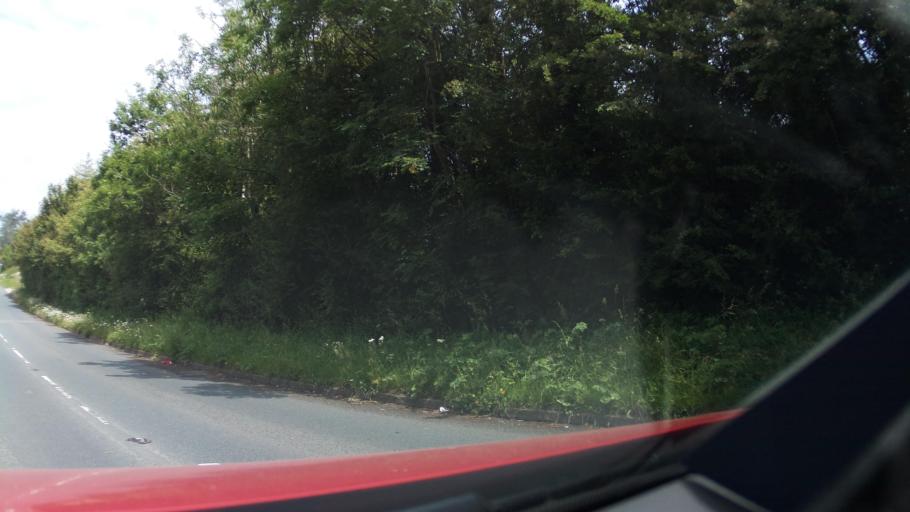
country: GB
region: Wales
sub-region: Vale of Glamorgan
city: Rhoose
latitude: 51.3996
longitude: -3.3900
